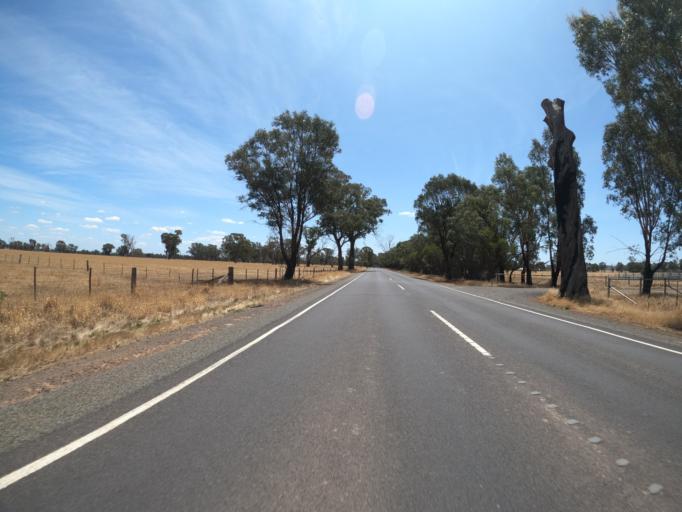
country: AU
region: Victoria
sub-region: Benalla
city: Benalla
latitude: -36.5078
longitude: 146.0266
